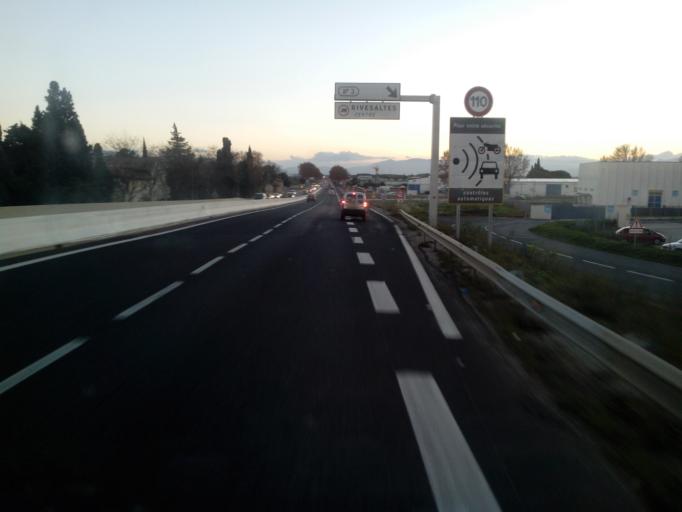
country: FR
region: Languedoc-Roussillon
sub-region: Departement des Pyrenees-Orientales
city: Rivesaltes
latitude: 42.7719
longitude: 2.9010
